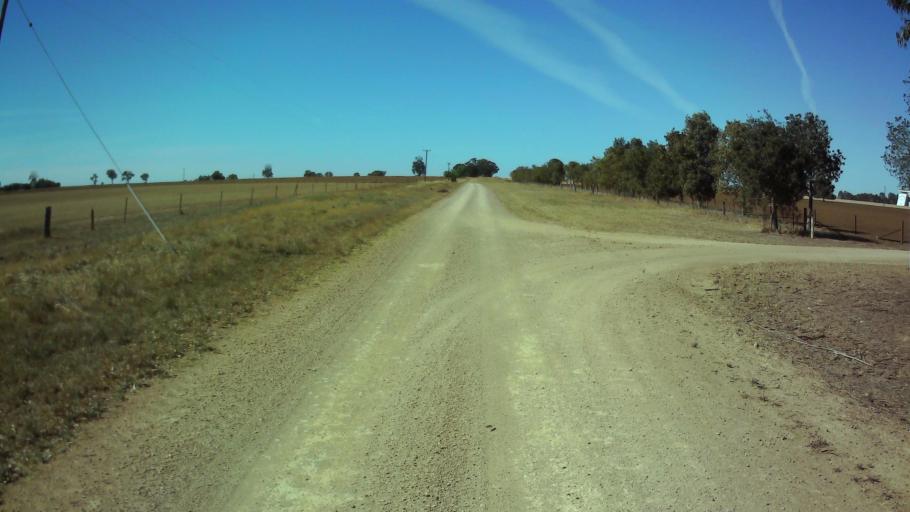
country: AU
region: New South Wales
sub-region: Weddin
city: Grenfell
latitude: -34.0580
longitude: 148.1714
